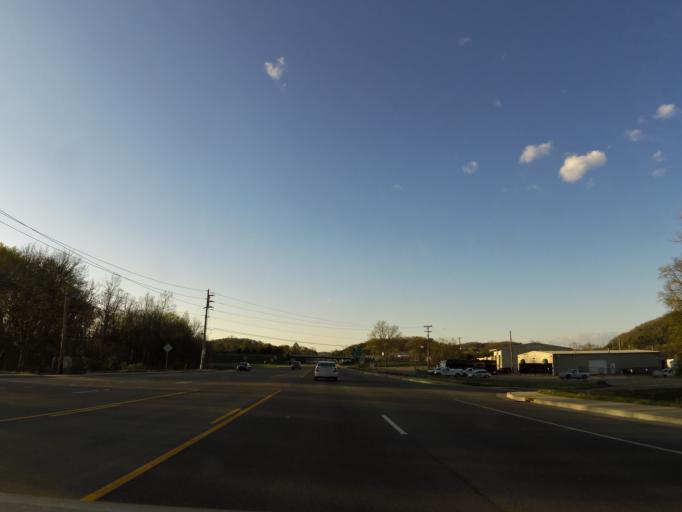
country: US
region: Tennessee
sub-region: Davidson County
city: Goodlettsville
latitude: 36.3398
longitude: -86.7182
